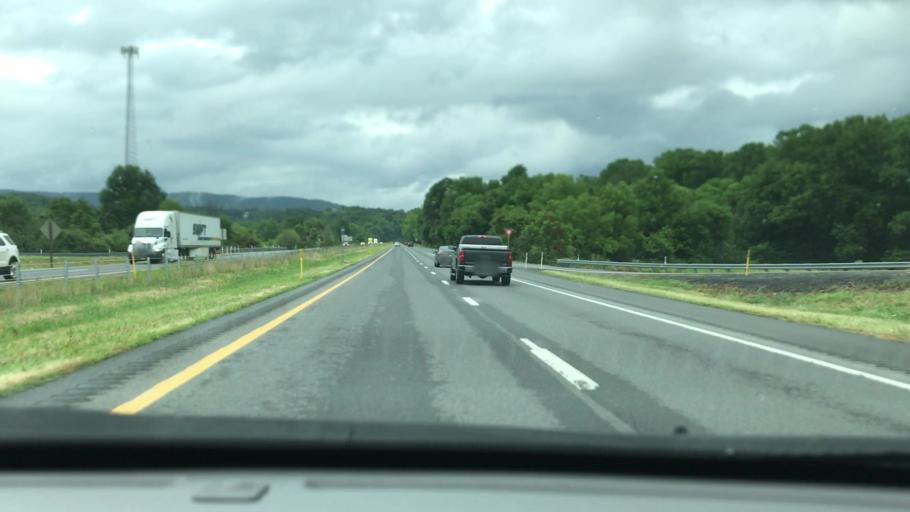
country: US
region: Maryland
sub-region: Washington County
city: Hancock
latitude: 39.7575
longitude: -78.1897
